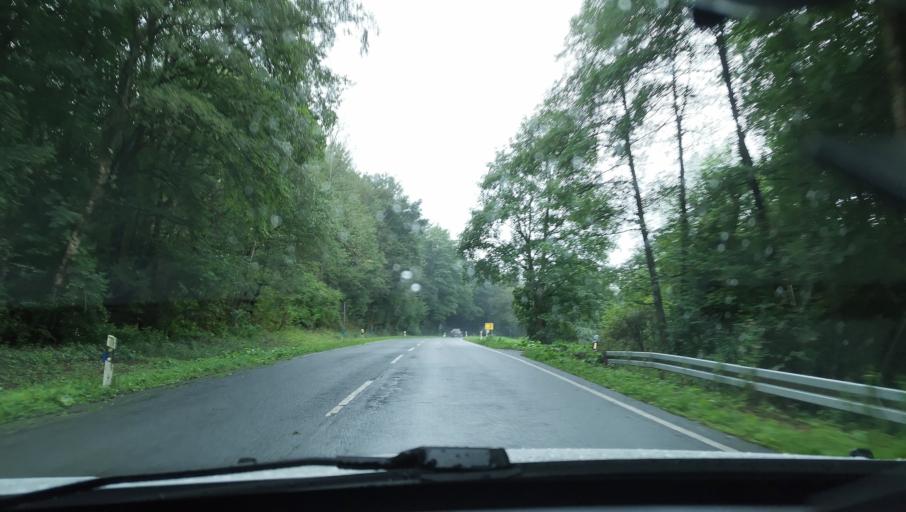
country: DE
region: North Rhine-Westphalia
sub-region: Regierungsbezirk Arnsberg
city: Breckerfeld
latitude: 51.2477
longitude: 7.4859
